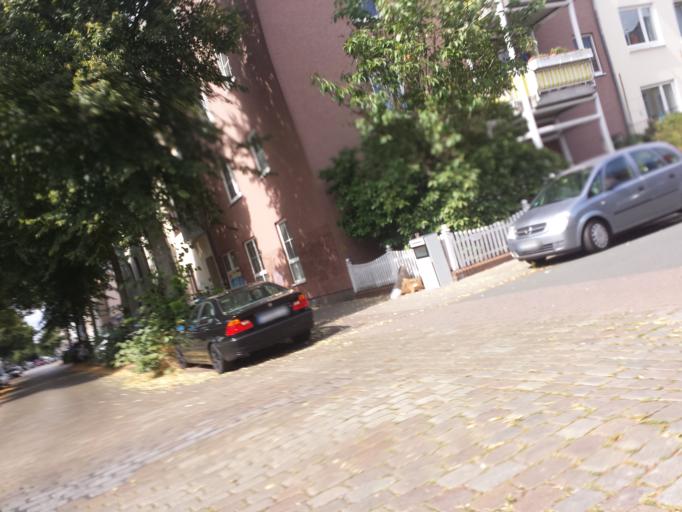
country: DE
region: Bremen
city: Bremen
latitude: 53.0677
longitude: 8.7869
